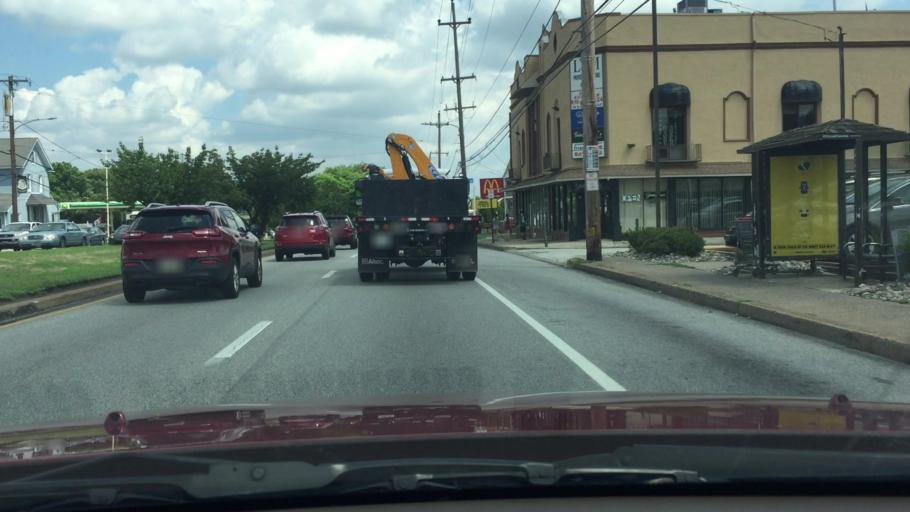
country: US
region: Pennsylvania
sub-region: Delaware County
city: Drexel Hill
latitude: 39.9729
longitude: -75.3193
